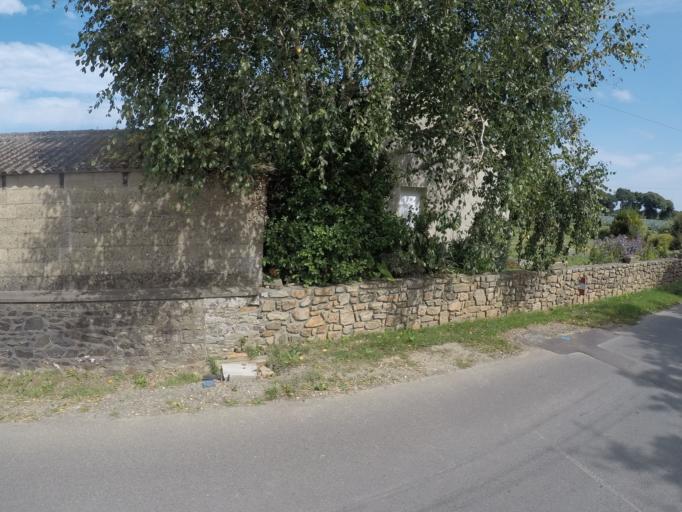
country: FR
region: Brittany
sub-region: Departement des Cotes-d'Armor
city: Goudelin
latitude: 48.5989
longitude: -3.0117
